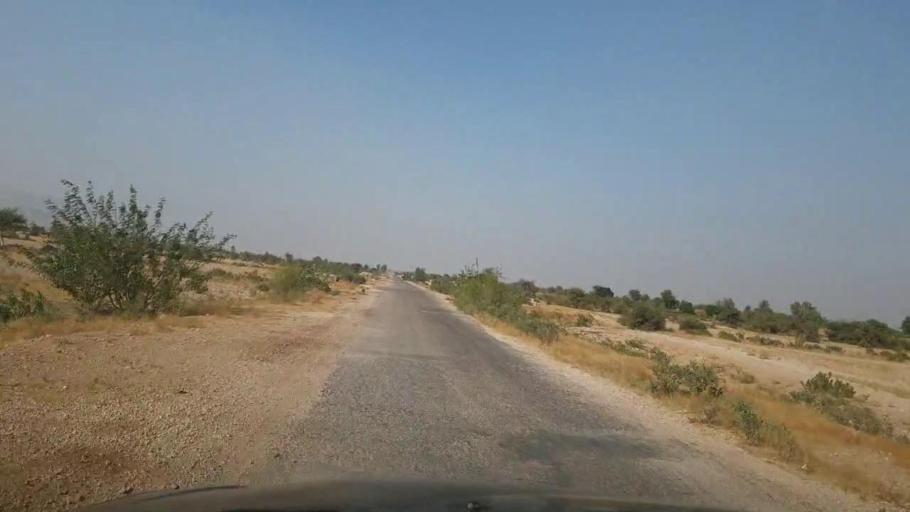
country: PK
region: Sindh
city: Jamshoro
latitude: 25.5864
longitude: 67.8199
